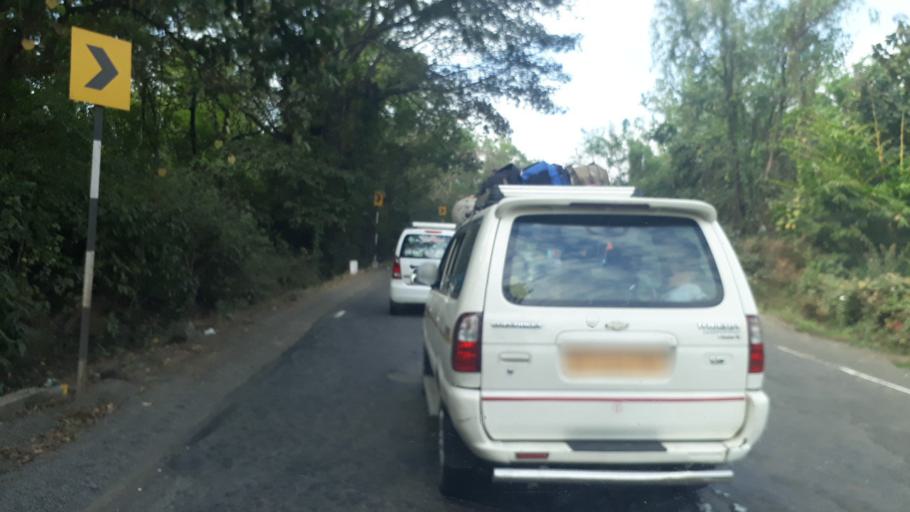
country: IN
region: Maharashtra
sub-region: Raigarh
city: Alibag
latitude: 18.6924
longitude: 72.9531
